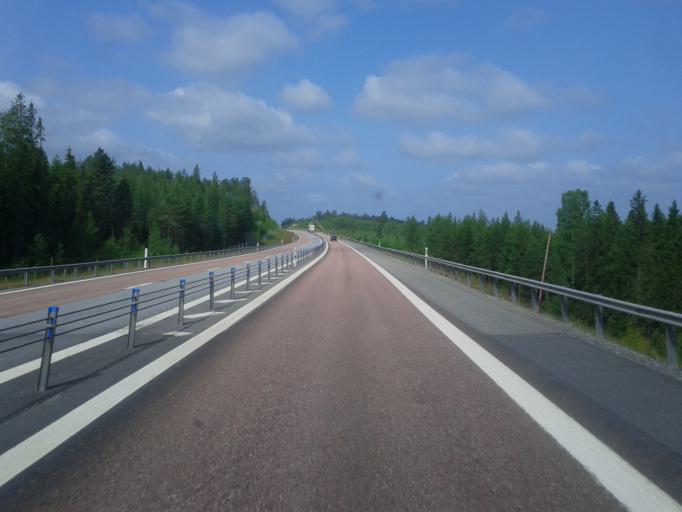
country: SE
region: Vaesterbotten
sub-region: Skelleftea Kommun
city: Soedra Bergsbyn
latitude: 64.6841
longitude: 21.0641
